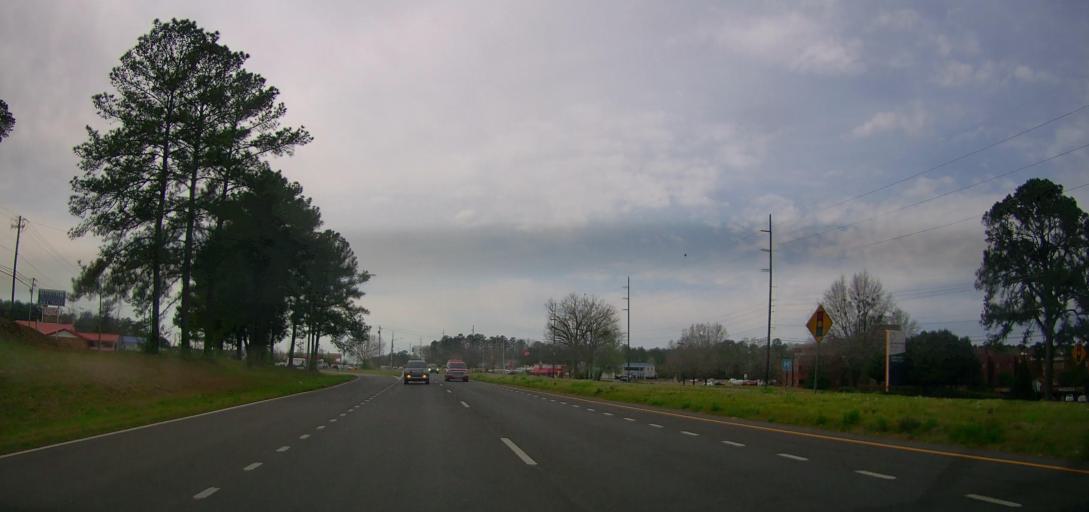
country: US
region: Alabama
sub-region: Walker County
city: Jasper
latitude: 33.8404
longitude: -87.2354
